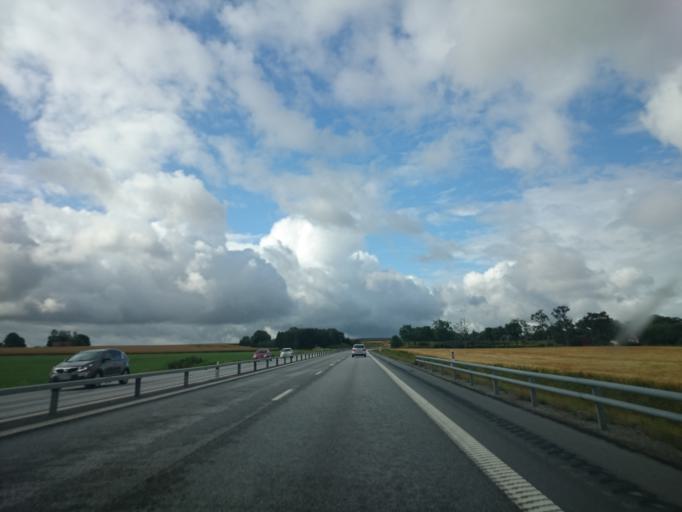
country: SE
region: Skane
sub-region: Hoors Kommun
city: Loberod
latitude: 55.7960
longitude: 13.4468
